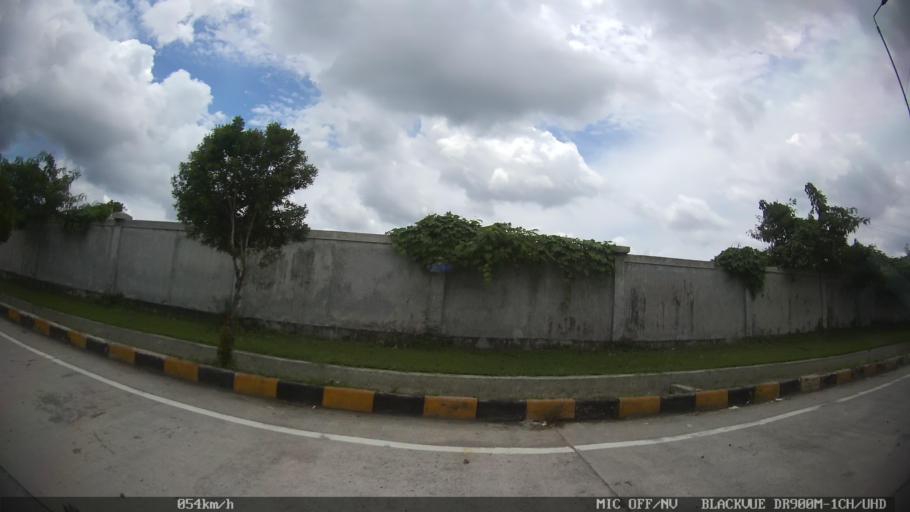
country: ID
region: North Sumatra
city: Medan
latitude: 3.6330
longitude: 98.7088
